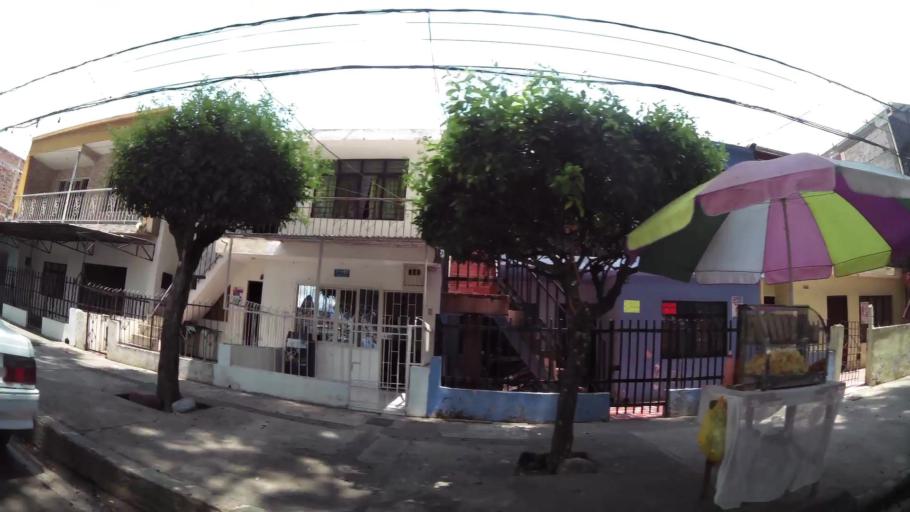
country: CO
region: Valle del Cauca
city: Cali
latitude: 3.4589
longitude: -76.4785
